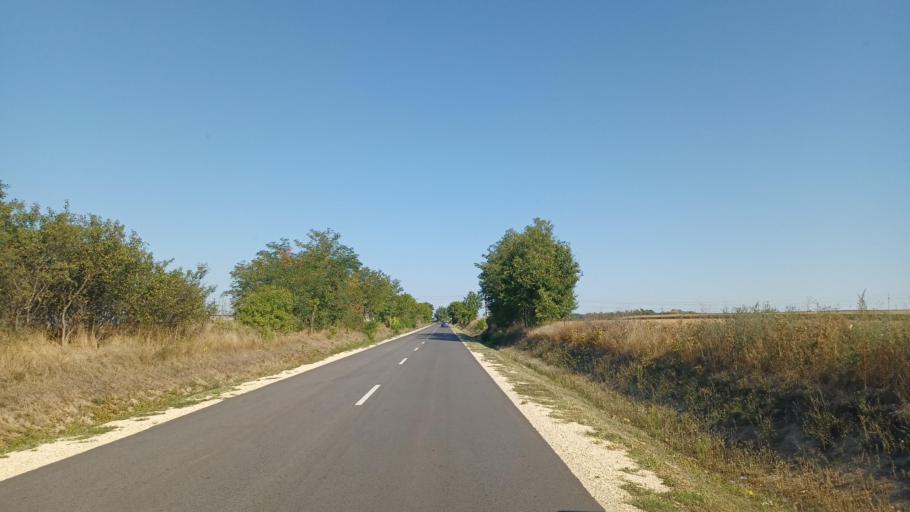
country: HU
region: Tolna
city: Paks
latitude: 46.6434
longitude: 18.8466
